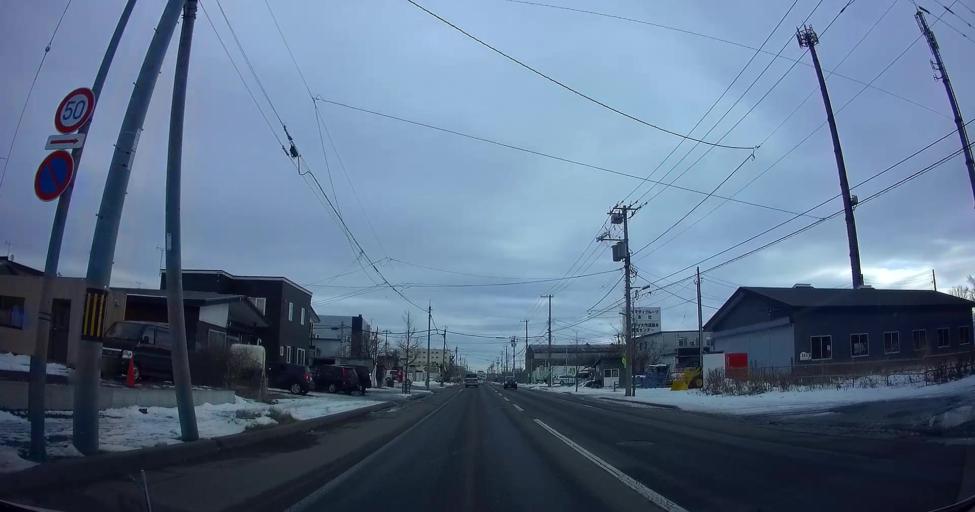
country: JP
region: Hokkaido
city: Hakodate
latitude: 41.8137
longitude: 140.7057
